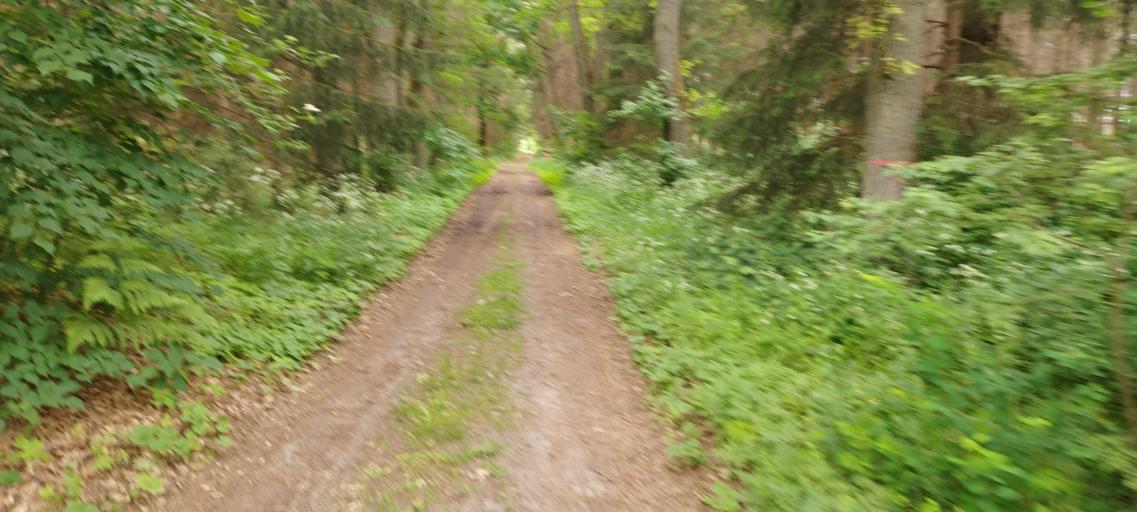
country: DE
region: Brandenburg
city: Spreenhagen
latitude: 52.4197
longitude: 13.8855
